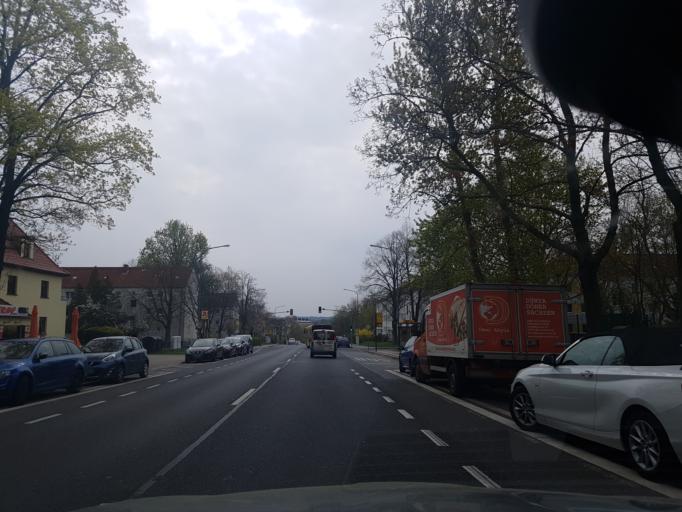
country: DE
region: Saxony
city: Albertstadt
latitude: 51.1169
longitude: 13.7694
